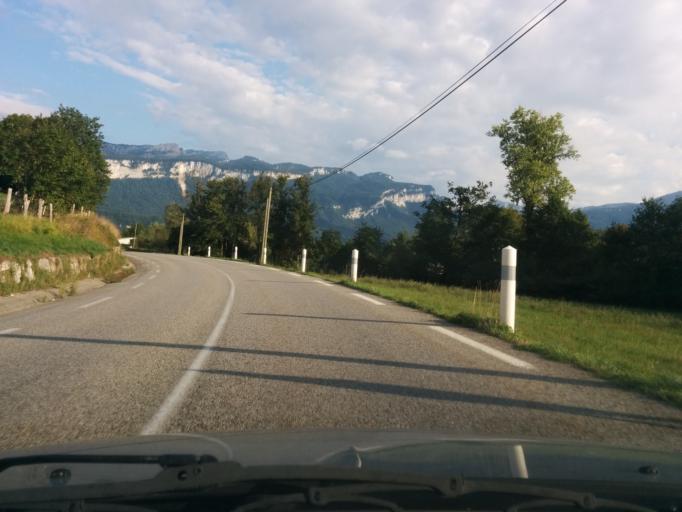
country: FR
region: Rhone-Alpes
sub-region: Departement de la Savoie
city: Les Echelles
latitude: 45.4464
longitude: 5.7385
